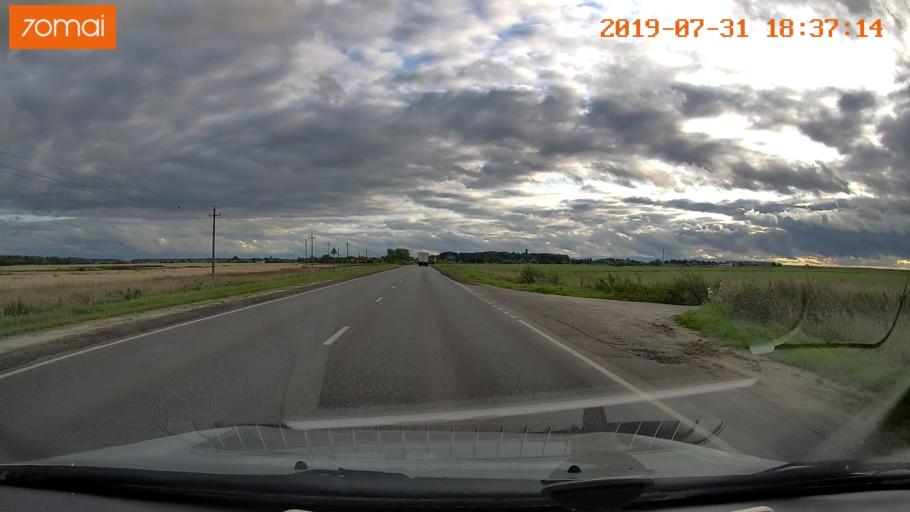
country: RU
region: Moskovskaya
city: Voskresensk
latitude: 55.2807
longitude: 38.6633
